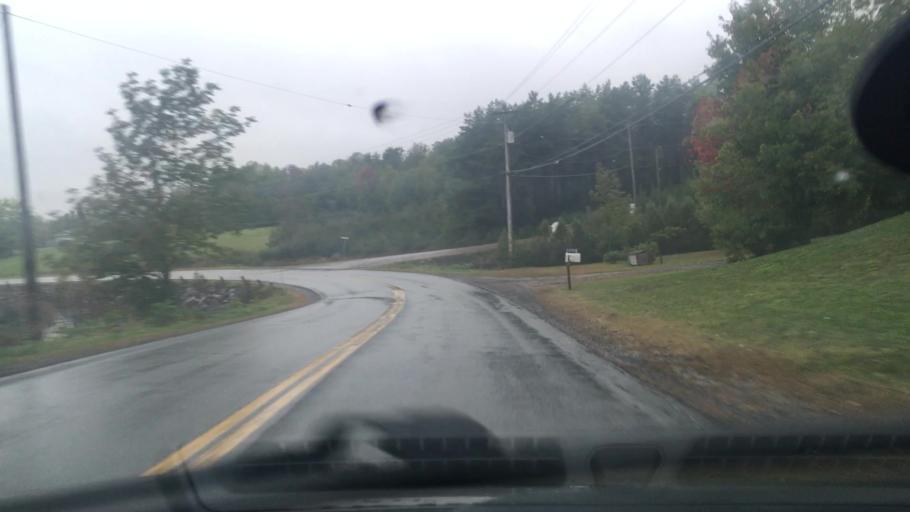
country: CA
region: Nova Scotia
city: Windsor
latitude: 44.8402
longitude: -64.2371
